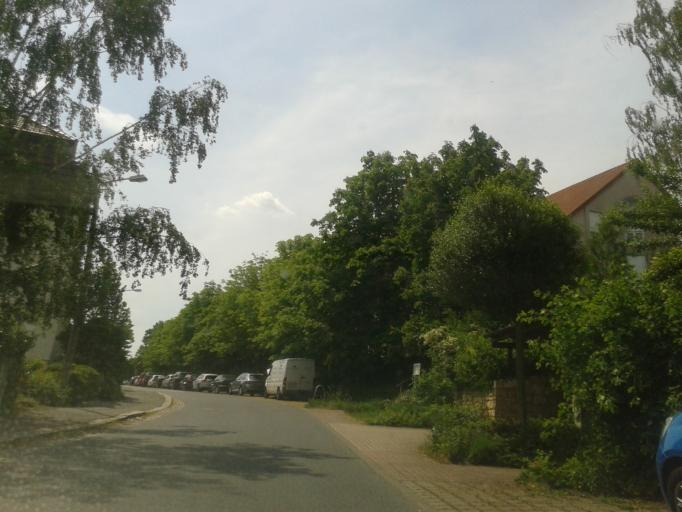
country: DE
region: Saxony
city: Bannewitz
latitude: 51.0012
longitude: 13.7256
